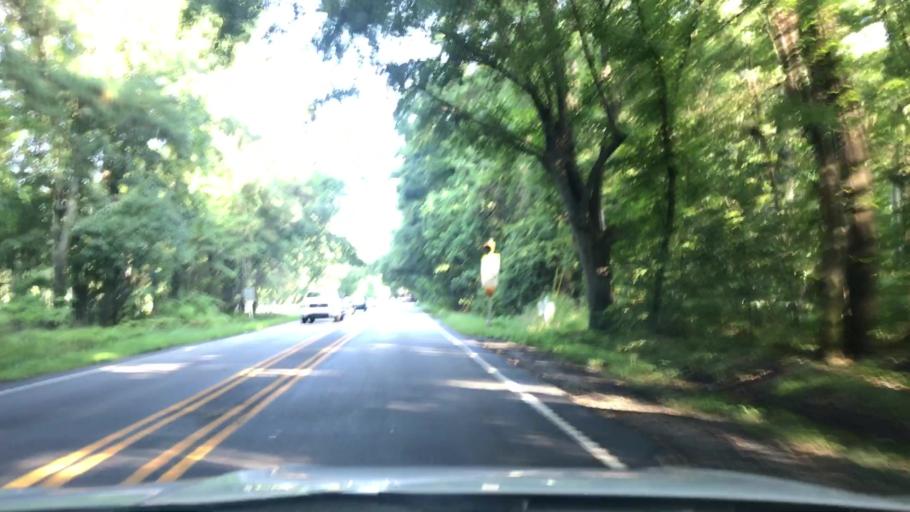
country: US
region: South Carolina
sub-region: Charleston County
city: Shell Point
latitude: 32.8537
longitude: -80.0700
